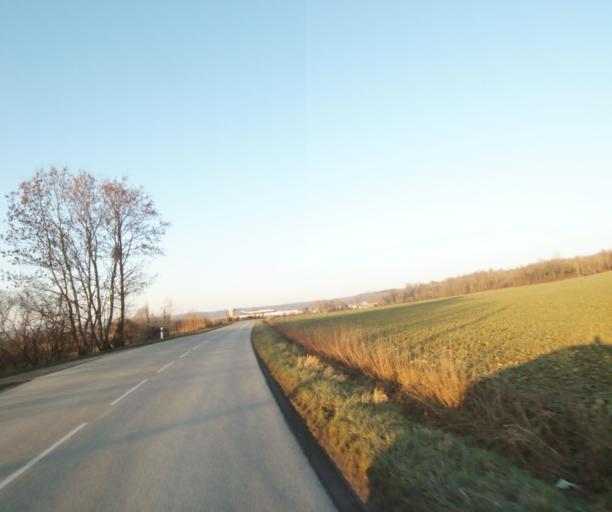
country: FR
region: Champagne-Ardenne
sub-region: Departement de la Haute-Marne
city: Bienville
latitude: 48.5934
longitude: 5.0416
